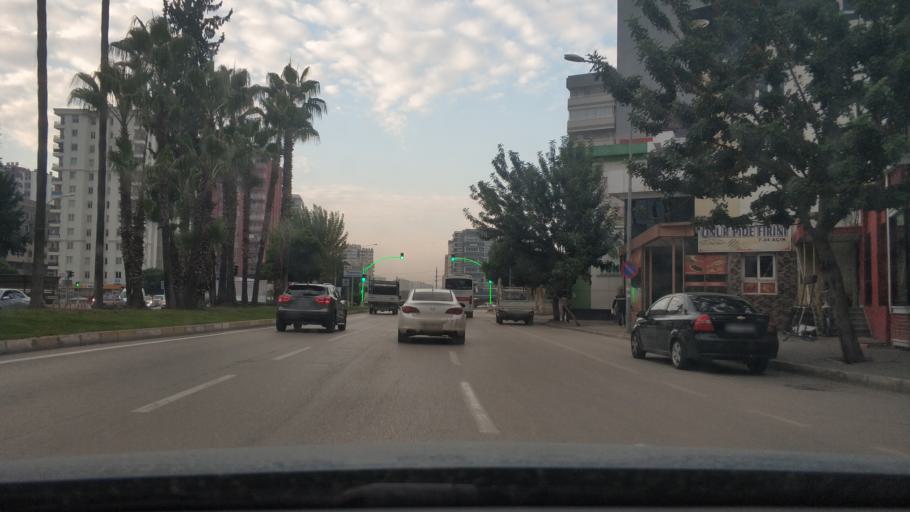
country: TR
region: Adana
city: Adana
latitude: 37.0010
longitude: 35.3147
